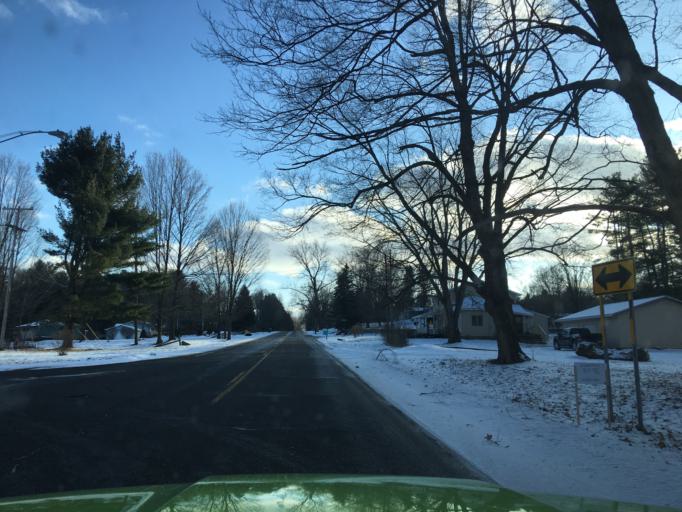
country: US
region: Michigan
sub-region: Montcalm County
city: Greenville
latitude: 43.1884
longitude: -85.2830
